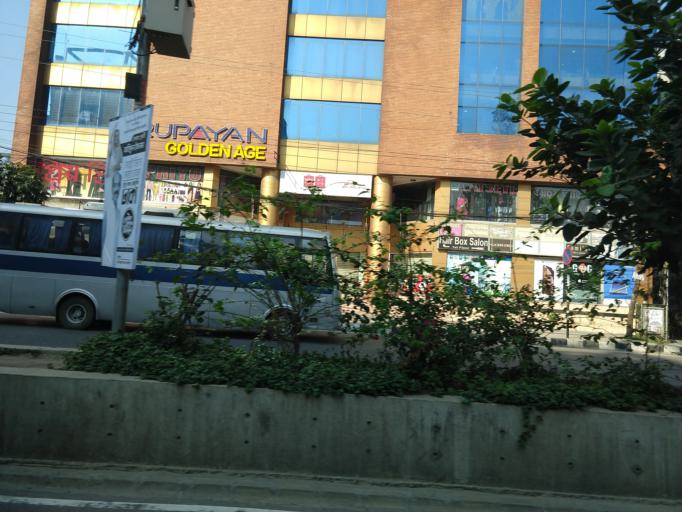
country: BD
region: Dhaka
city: Paltan
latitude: 23.7884
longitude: 90.4165
